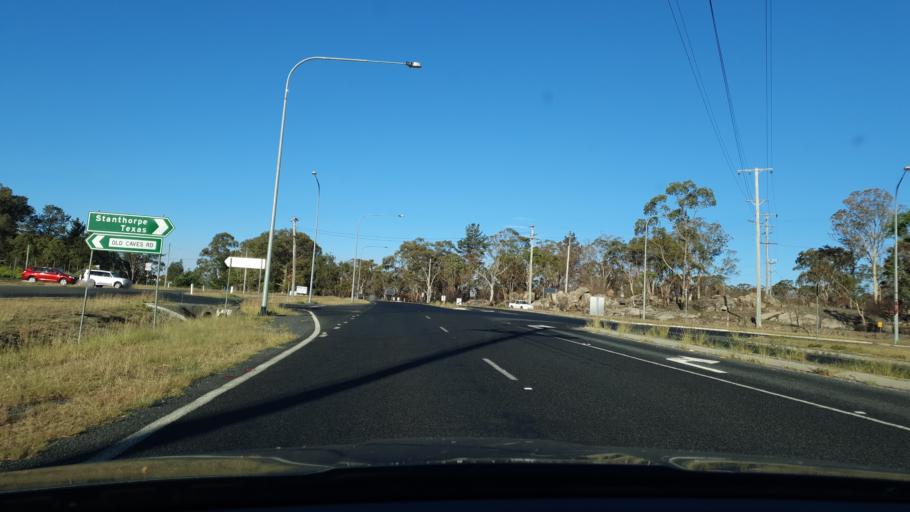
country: AU
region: Queensland
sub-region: Southern Downs
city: Stanthorpe
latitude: -28.6359
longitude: 151.9503
